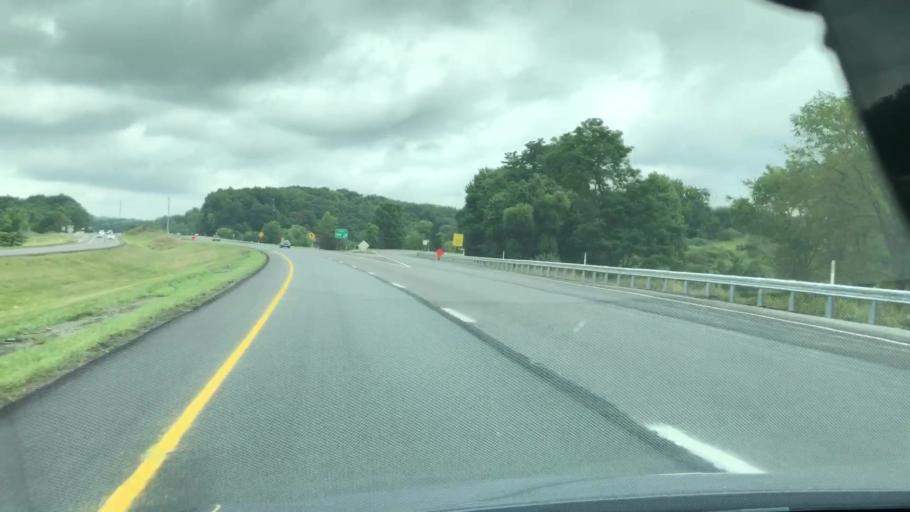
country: US
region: Pennsylvania
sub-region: Butler County
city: Prospect
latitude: 40.9591
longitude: -80.1359
